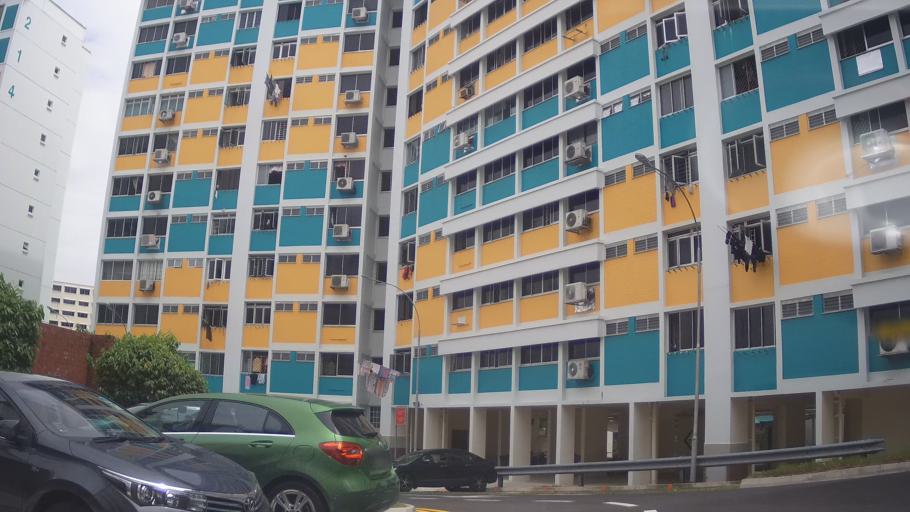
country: MY
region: Johor
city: Johor Bahru
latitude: 1.3742
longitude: 103.7753
